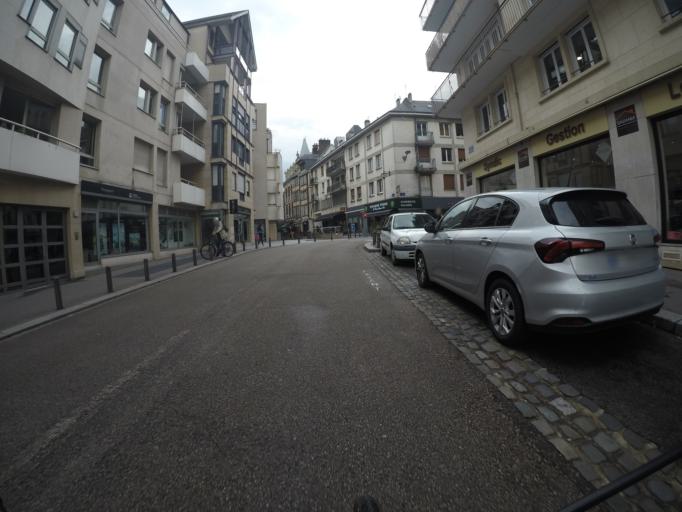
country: FR
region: Haute-Normandie
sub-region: Departement de la Seine-Maritime
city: Rouen
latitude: 49.4412
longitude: 1.0888
